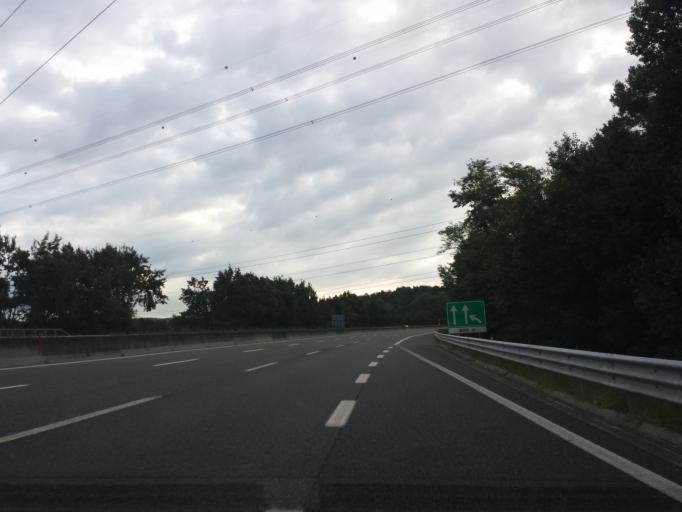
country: IT
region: Lombardy
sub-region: Provincia di Varese
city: Vergiate
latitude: 45.7201
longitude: 8.6717
